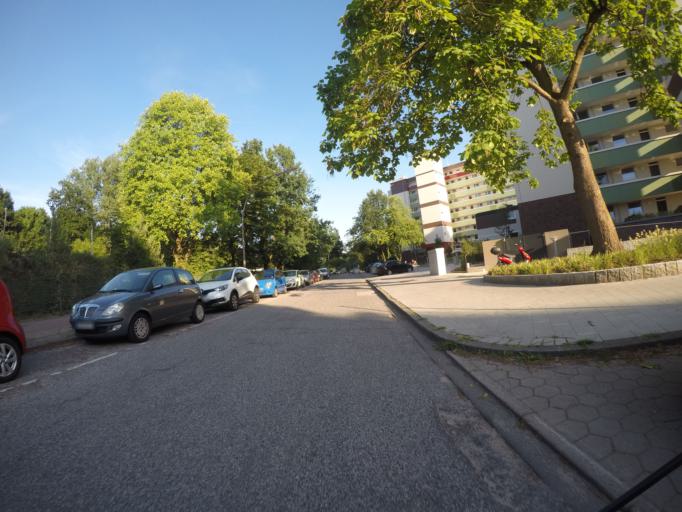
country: DE
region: Schleswig-Holstein
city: Halstenbek
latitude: 53.5763
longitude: 9.8138
